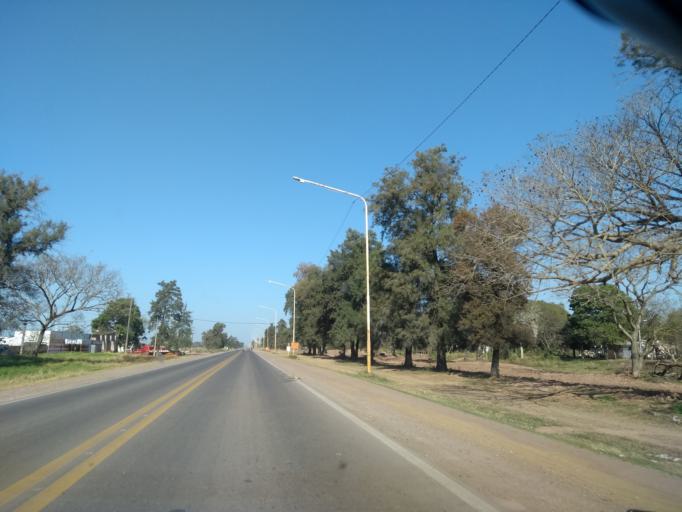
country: AR
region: Chaco
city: Presidencia Roque Saenz Pena
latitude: -26.7934
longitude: -60.4100
